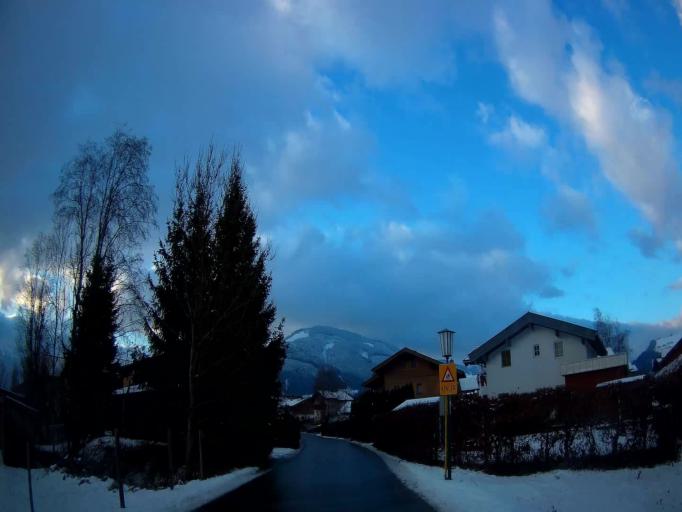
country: AT
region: Salzburg
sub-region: Politischer Bezirk Zell am See
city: Saalfelden am Steinernen Meer
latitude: 47.4514
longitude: 12.8202
